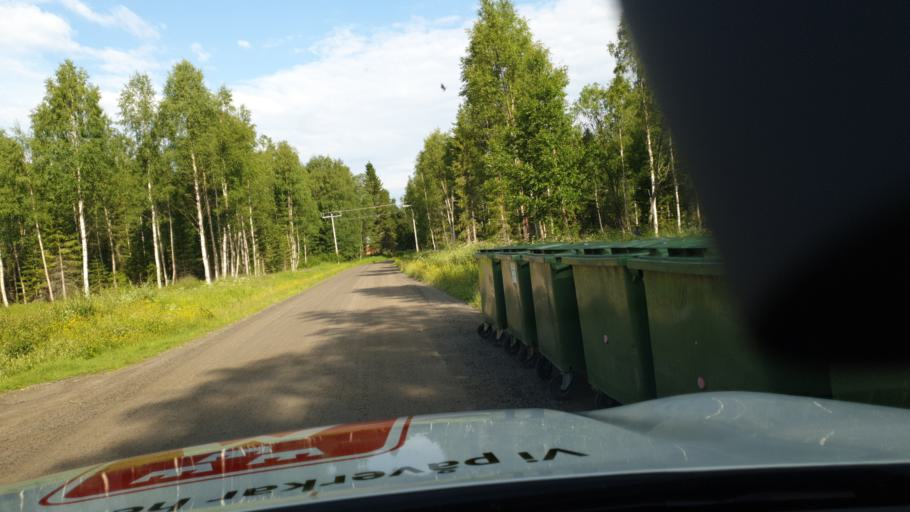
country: SE
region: Vaesterbotten
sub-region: Robertsfors Kommun
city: Robertsfors
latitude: 64.2174
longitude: 21.0761
